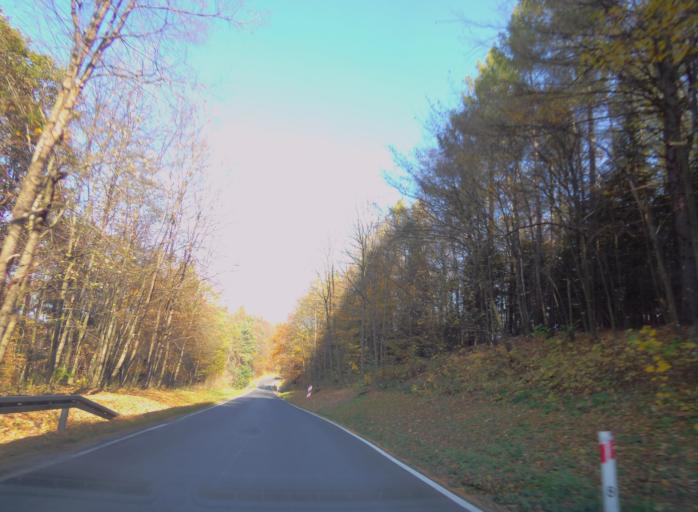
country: PL
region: Subcarpathian Voivodeship
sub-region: Powiat leski
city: Polanczyk
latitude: 49.3970
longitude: 22.4393
